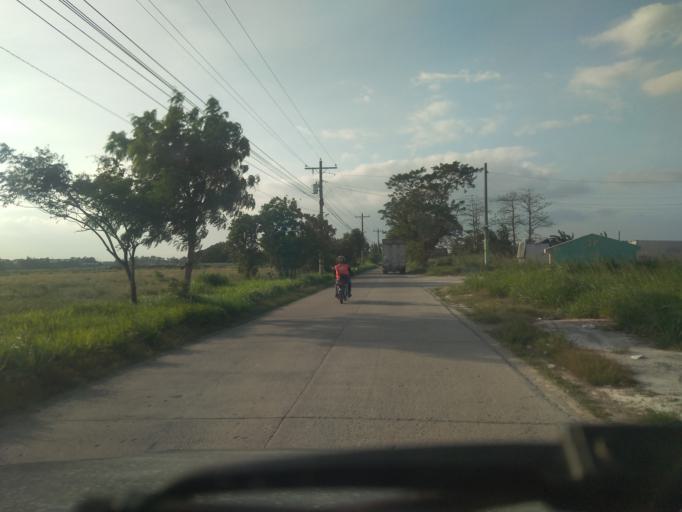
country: PH
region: Central Luzon
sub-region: Province of Pampanga
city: Malino
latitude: 15.1069
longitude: 120.6712
